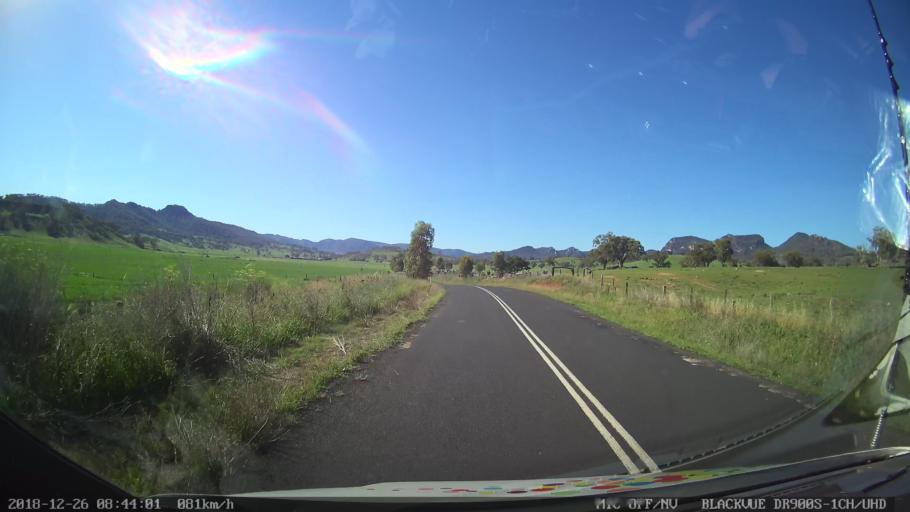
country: AU
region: New South Wales
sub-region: Mid-Western Regional
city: Kandos
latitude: -32.5091
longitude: 150.0804
